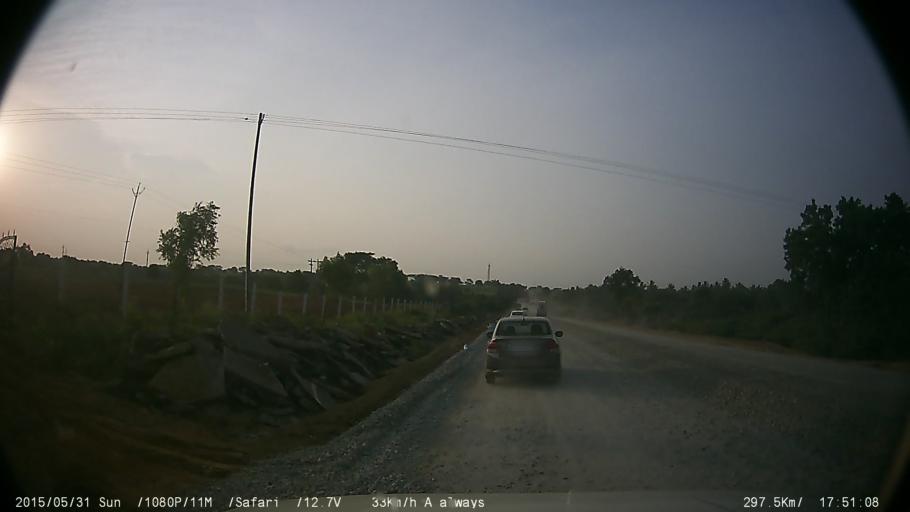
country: IN
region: Karnataka
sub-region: Mysore
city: Nanjangud
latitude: 11.9763
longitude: 76.6696
